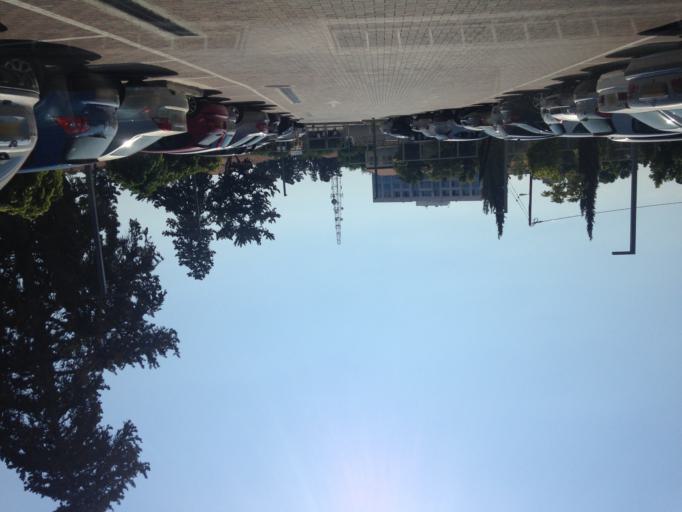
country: CY
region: Pafos
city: Paphos
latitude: 34.7761
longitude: 32.4235
